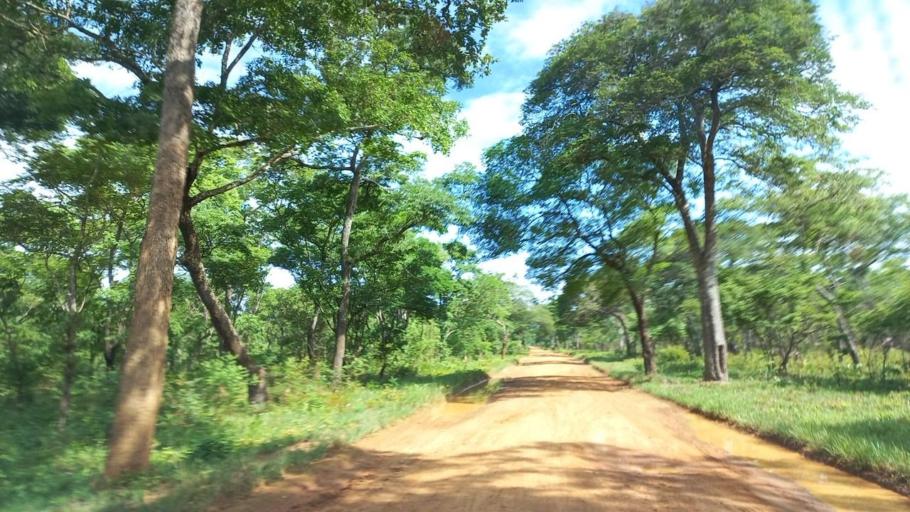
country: ZM
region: North-Western
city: Kabompo
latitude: -13.0842
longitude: 24.2203
